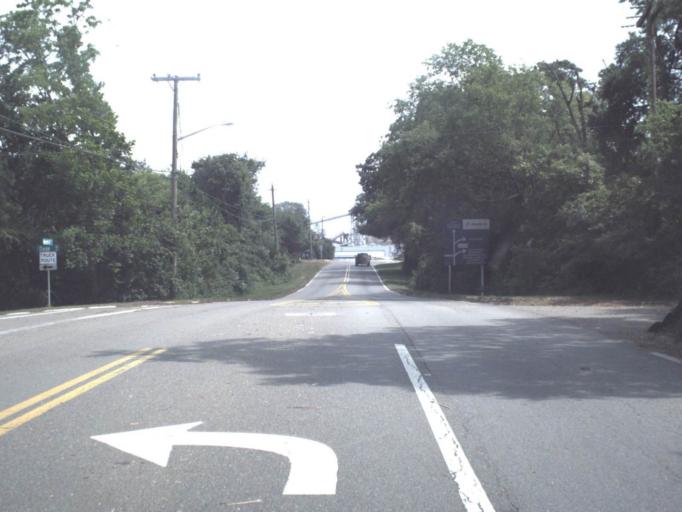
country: US
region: Florida
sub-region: Nassau County
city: Fernandina Beach
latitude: 30.6756
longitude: -81.4581
